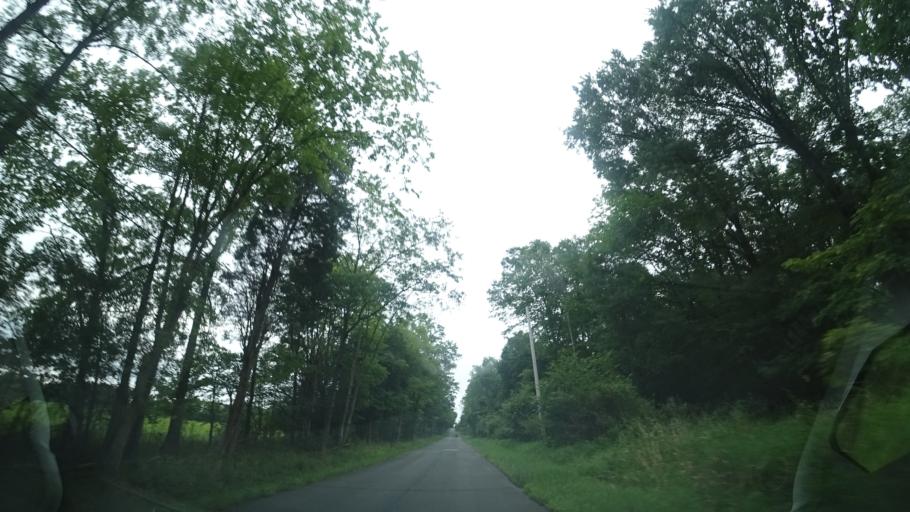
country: US
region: Maryland
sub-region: Montgomery County
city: Poolesville
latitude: 39.1121
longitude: -77.4451
